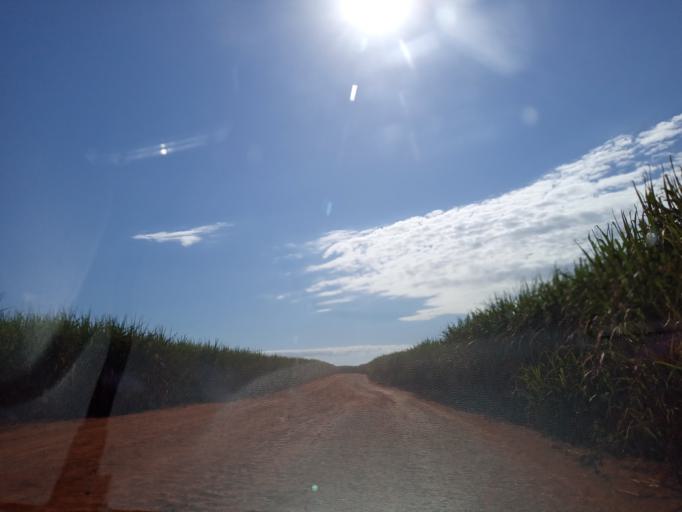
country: BR
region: Goias
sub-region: Itumbiara
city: Itumbiara
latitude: -18.4503
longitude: -49.1813
